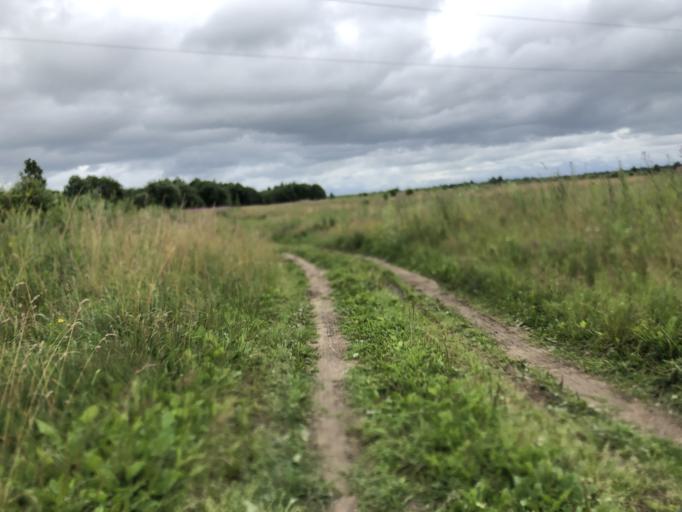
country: RU
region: Tverskaya
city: Rzhev
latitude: 56.2401
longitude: 34.3795
